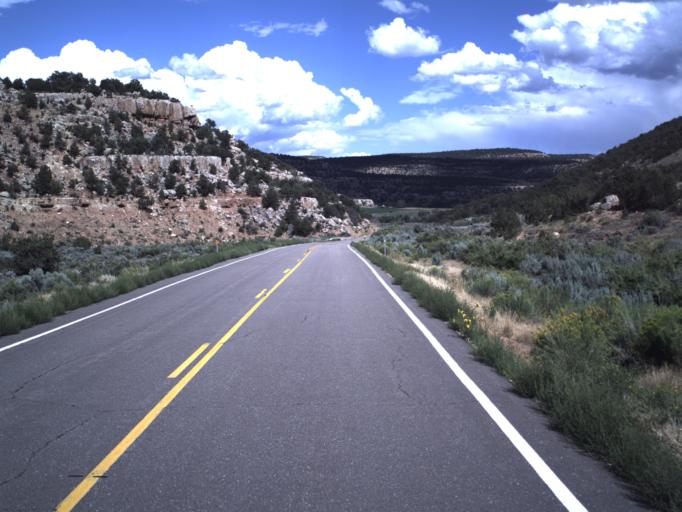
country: US
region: Utah
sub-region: Duchesne County
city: Duchesne
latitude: 40.3218
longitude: -110.6846
